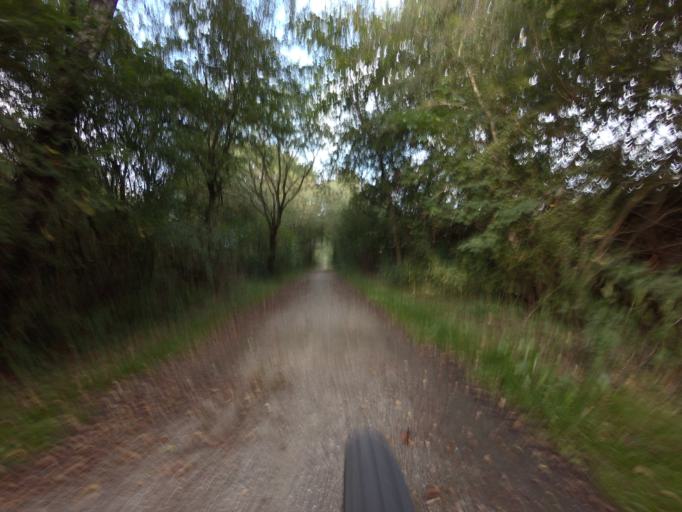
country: DK
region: Central Jutland
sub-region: Ikast-Brande Kommune
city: Brande
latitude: 55.9118
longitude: 9.0917
